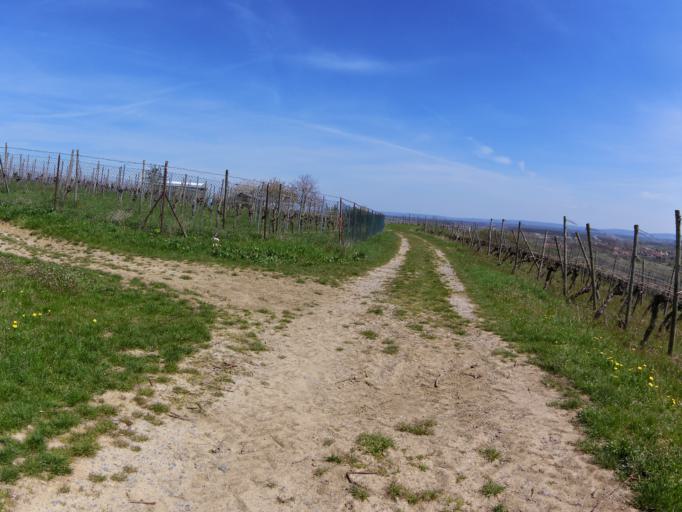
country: DE
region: Bavaria
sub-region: Regierungsbezirk Unterfranken
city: Mainstockheim
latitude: 49.7957
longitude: 10.1504
